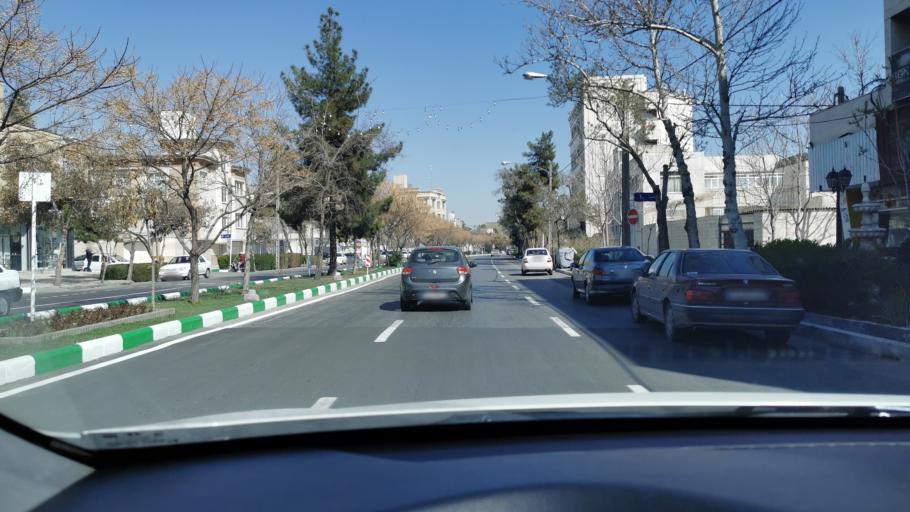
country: IR
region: Razavi Khorasan
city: Mashhad
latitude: 36.2924
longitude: 59.5722
